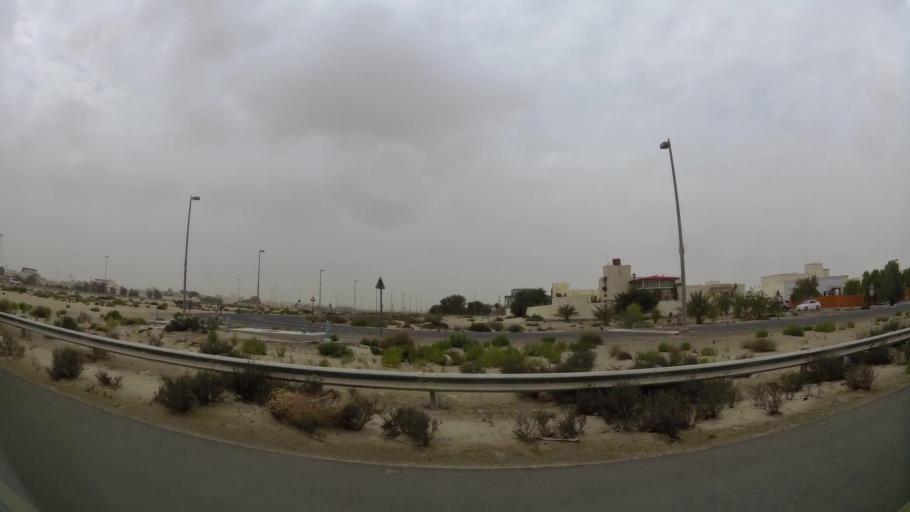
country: AE
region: Abu Dhabi
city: Abu Dhabi
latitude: 24.4058
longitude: 54.7455
